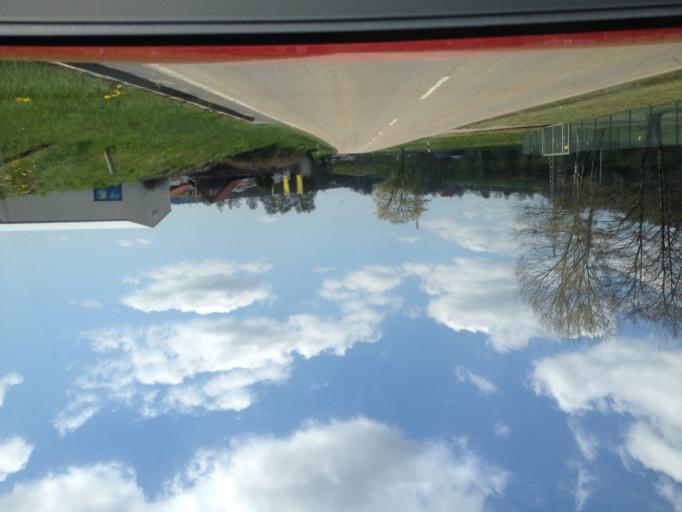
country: DE
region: Bavaria
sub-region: Upper Palatinate
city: Waldershof
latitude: 49.9861
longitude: 12.0711
